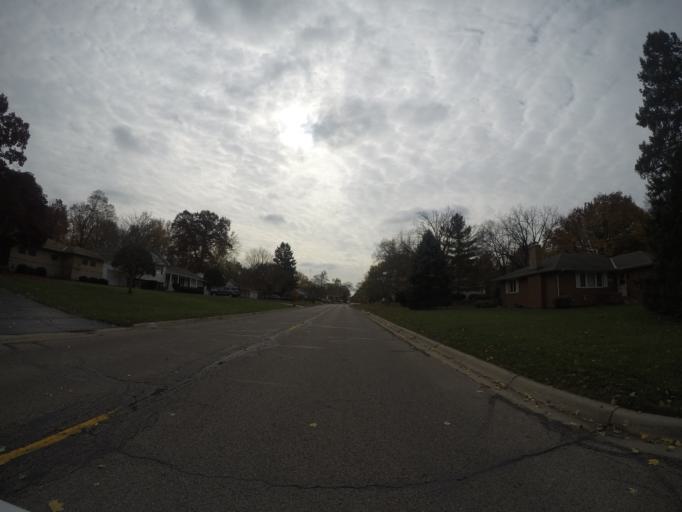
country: US
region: Ohio
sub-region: Franklin County
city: Upper Arlington
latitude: 40.0199
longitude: -83.0478
